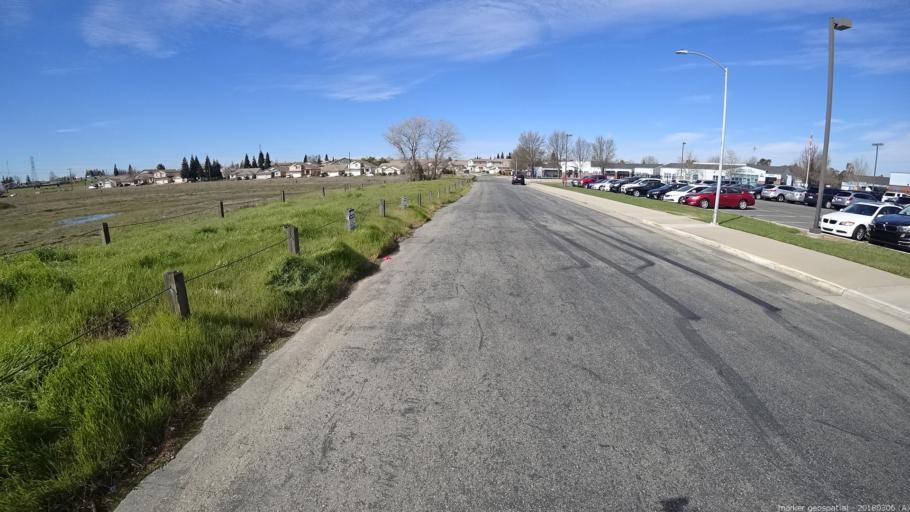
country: US
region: California
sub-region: Sacramento County
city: Vineyard
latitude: 38.4653
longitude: -121.3398
